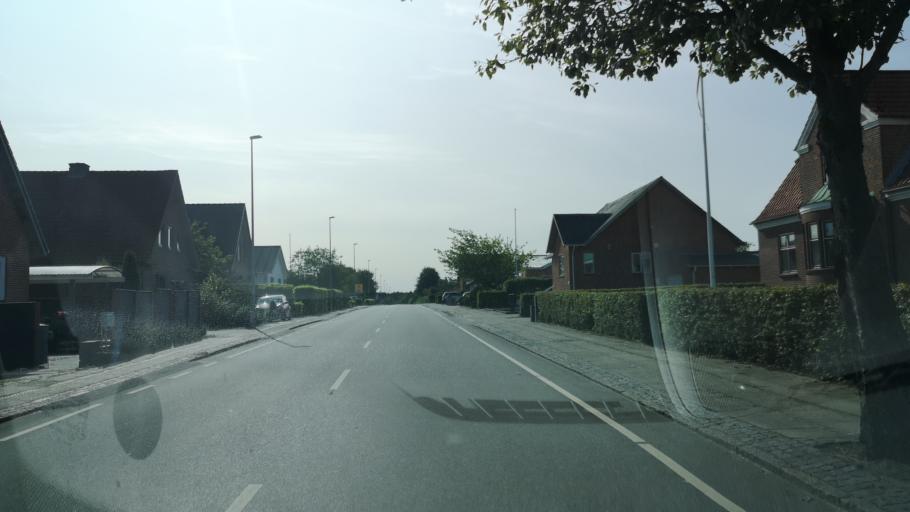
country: DK
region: Central Jutland
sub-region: Ringkobing-Skjern Kommune
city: Videbaek
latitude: 56.0878
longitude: 8.6293
